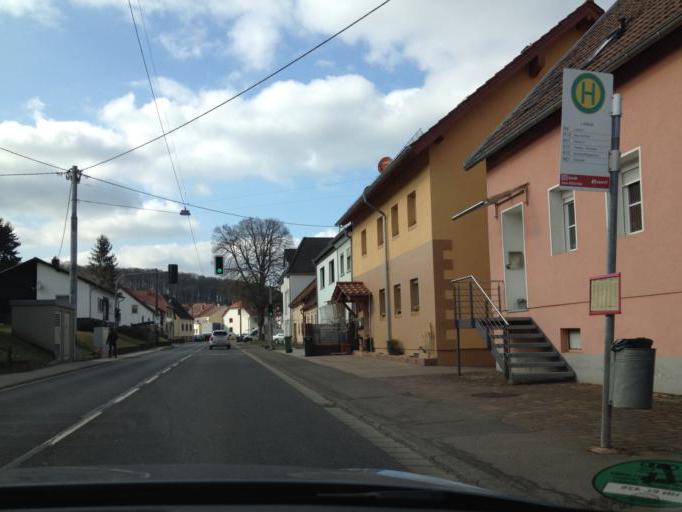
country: DE
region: Saarland
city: Oberthal
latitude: 49.4706
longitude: 7.1037
